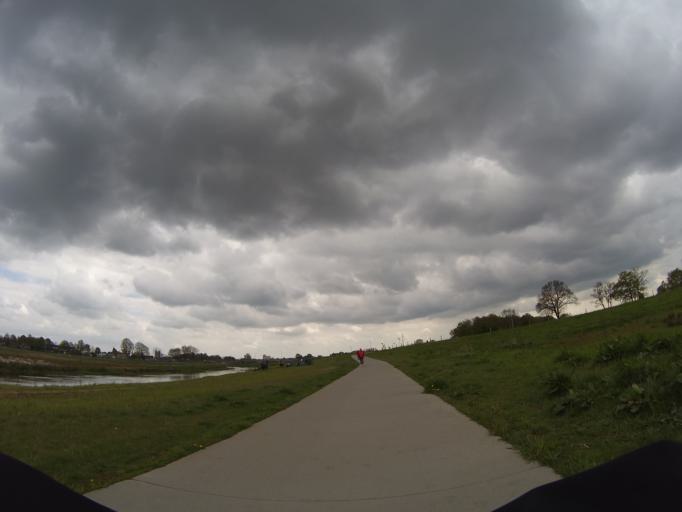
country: NL
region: Overijssel
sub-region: Gemeente Hardenberg
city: Hardenberg
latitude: 52.5680
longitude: 6.6125
